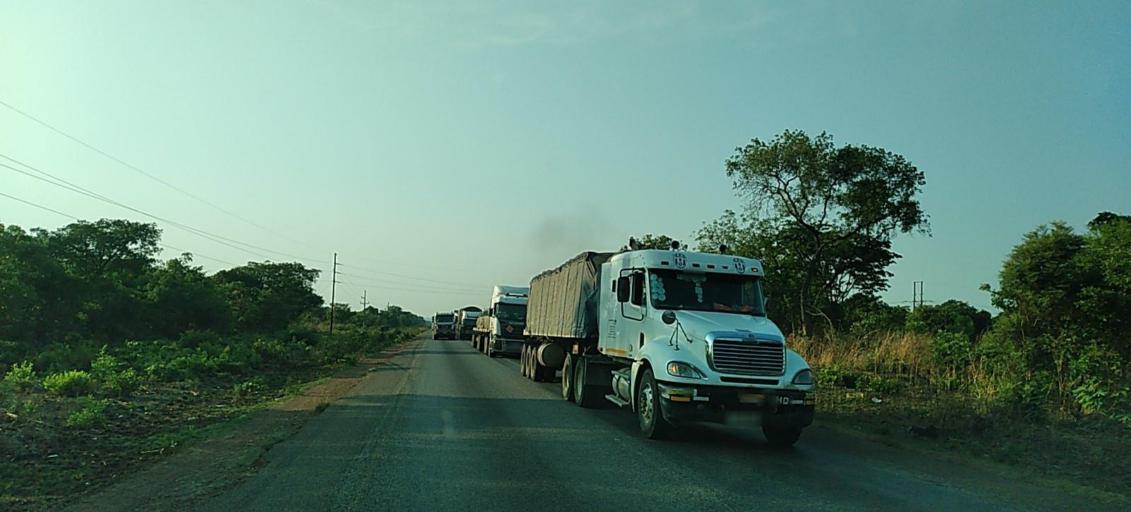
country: ZM
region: Copperbelt
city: Luanshya
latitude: -13.2641
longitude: 28.6782
